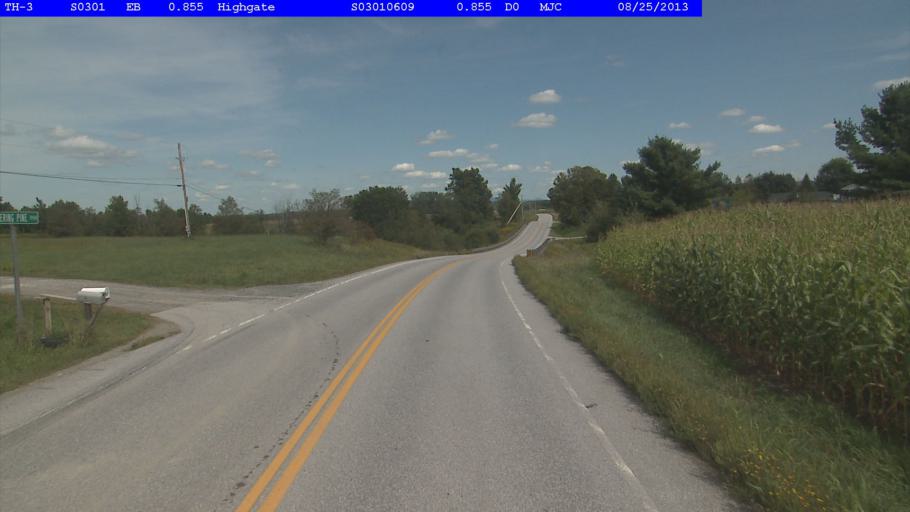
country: US
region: Vermont
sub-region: Franklin County
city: Swanton
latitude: 44.9546
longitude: -73.0020
